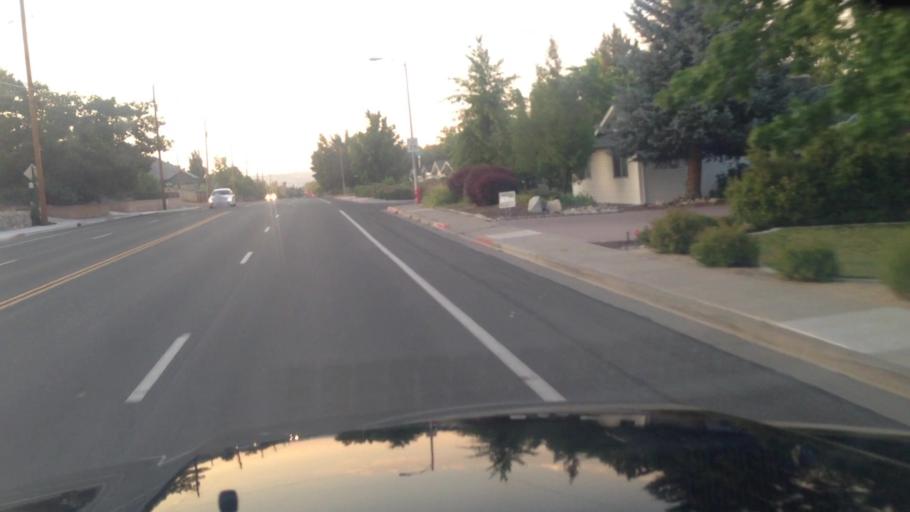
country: US
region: Nevada
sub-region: Washoe County
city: Reno
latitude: 39.4843
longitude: -119.8079
